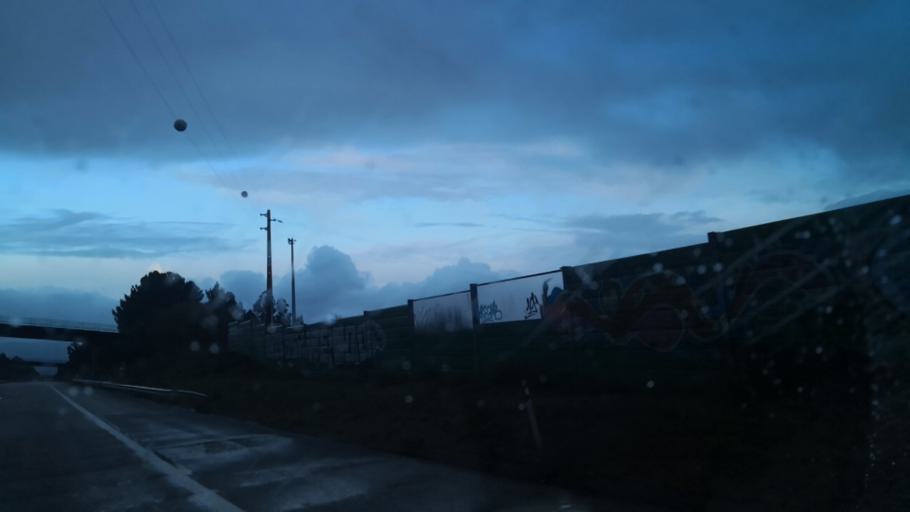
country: PT
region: Viana do Castelo
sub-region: Vila Nova de Cerveira
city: Vila Nova de Cerveira
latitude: 41.9454
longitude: -8.6648
